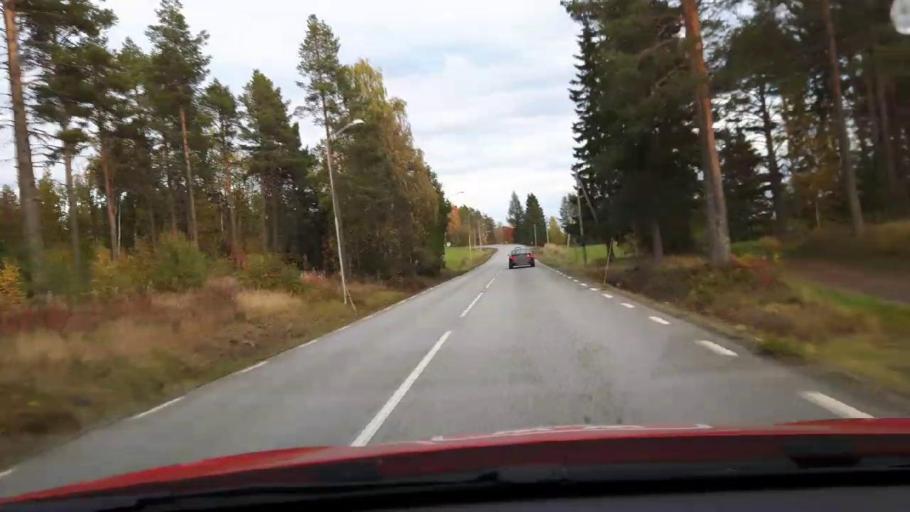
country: SE
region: Jaemtland
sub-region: Krokoms Kommun
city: Krokom
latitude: 63.3575
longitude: 14.5011
